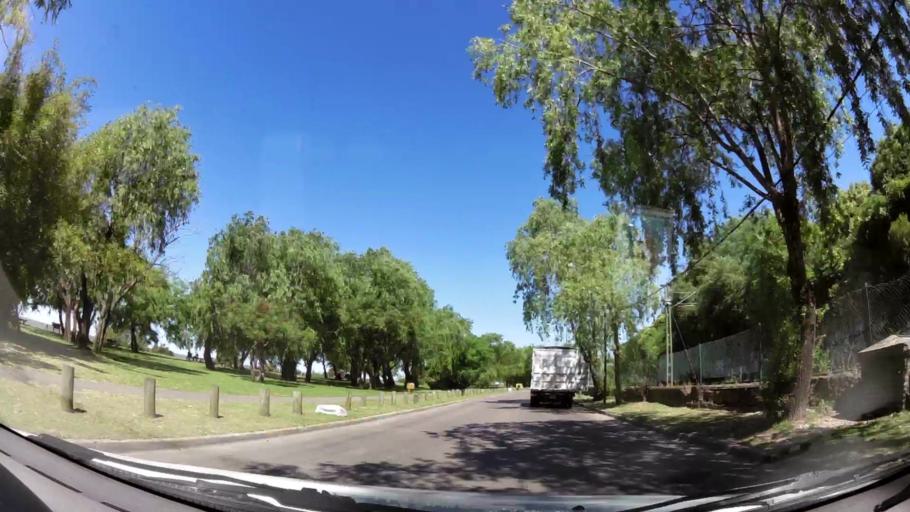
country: AR
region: Buenos Aires
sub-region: Partido de San Isidro
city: San Isidro
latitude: -34.4763
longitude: -58.4859
